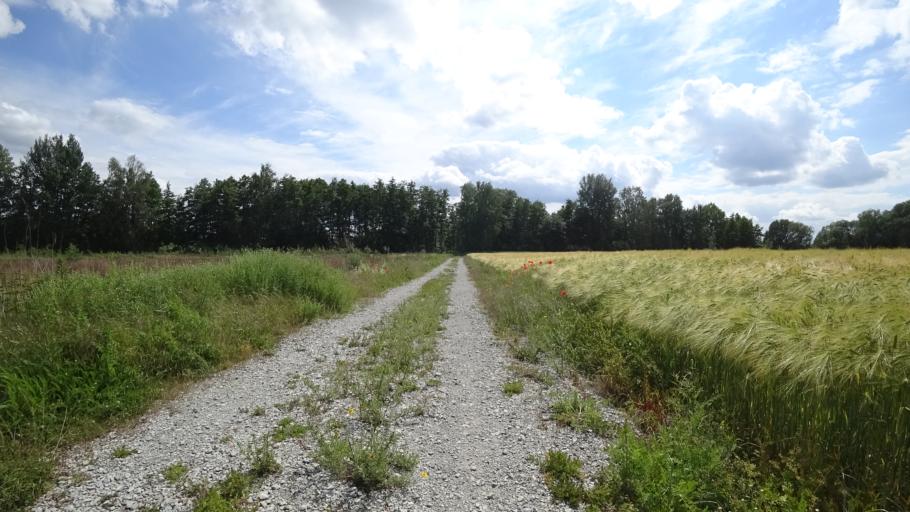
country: DE
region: North Rhine-Westphalia
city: Rietberg
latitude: 51.8127
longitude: 8.4157
